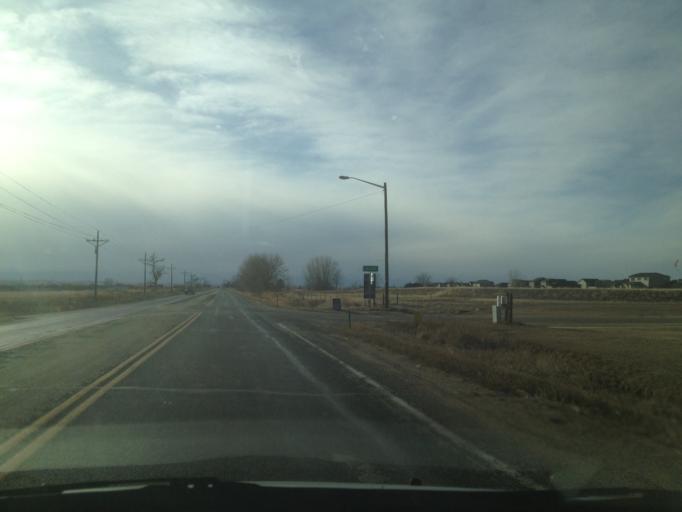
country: US
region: Colorado
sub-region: Weld County
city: Fort Lupton
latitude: 40.0803
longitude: -104.7816
